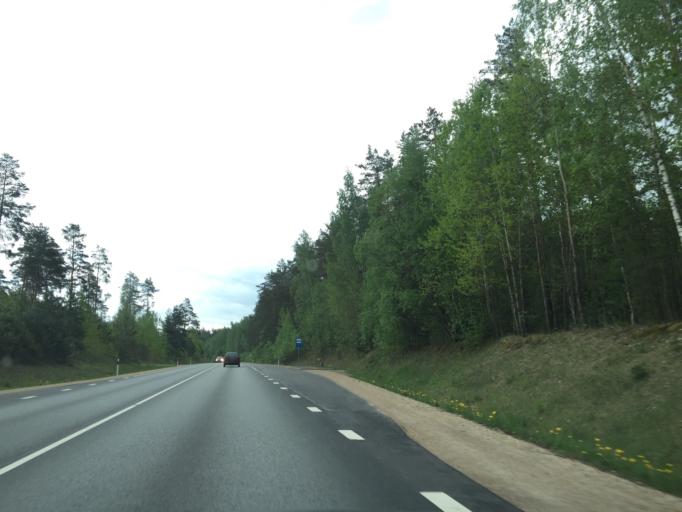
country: LV
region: Ikskile
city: Ikskile
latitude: 56.8937
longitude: 24.4462
